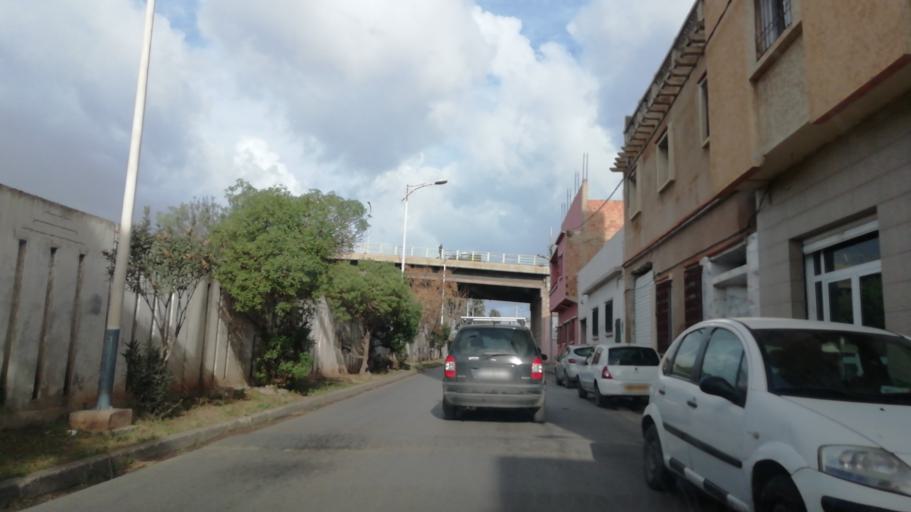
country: DZ
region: Oran
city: Oran
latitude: 35.6845
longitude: -0.6284
